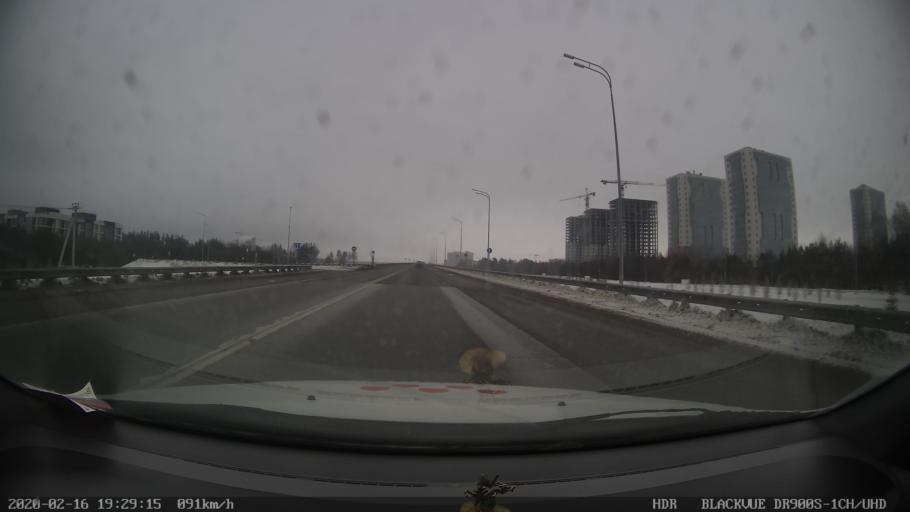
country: RU
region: Tatarstan
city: Stolbishchi
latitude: 55.6794
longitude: 49.1919
